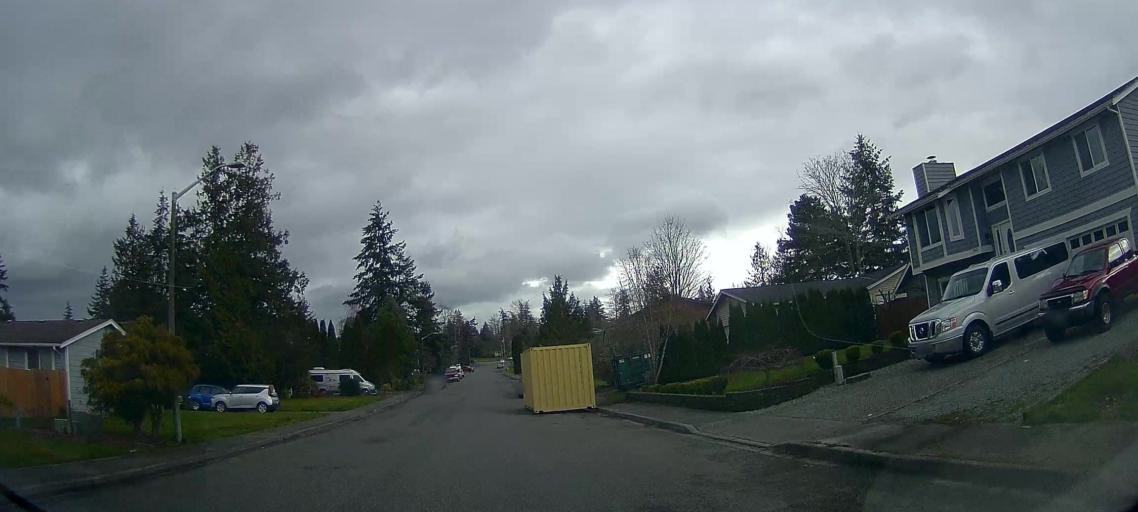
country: US
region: Washington
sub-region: Skagit County
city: Mount Vernon
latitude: 48.4407
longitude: -122.3175
